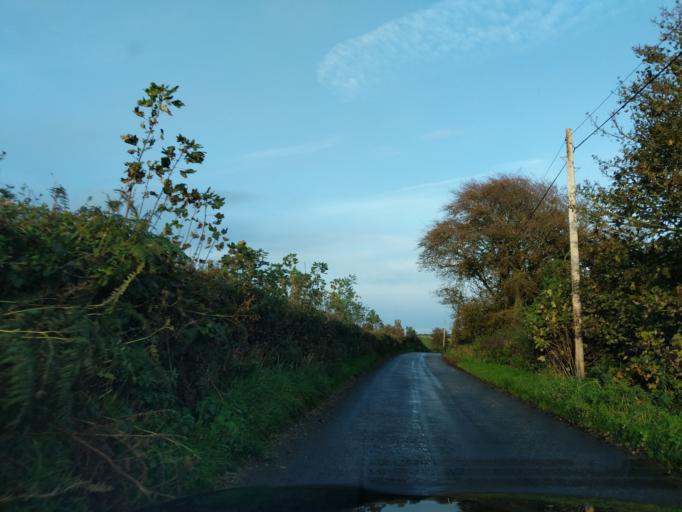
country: GB
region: Scotland
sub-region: Dumfries and Galloway
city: Kirkcudbright
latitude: 54.8117
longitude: -4.1682
